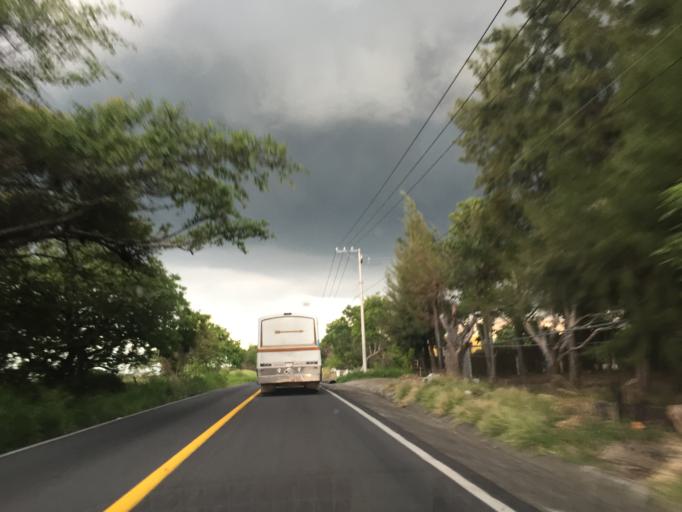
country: MX
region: Colima
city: Cuauhtemoc
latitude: 19.3380
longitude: -103.5878
